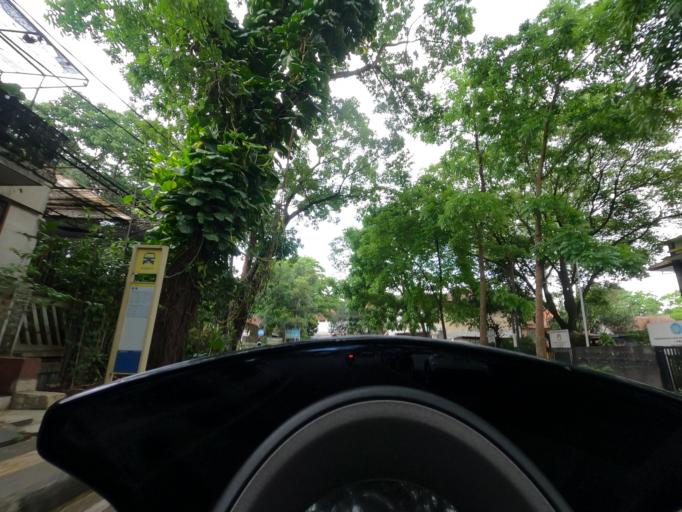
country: ID
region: West Java
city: Bandung
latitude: -6.9133
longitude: 107.6178
